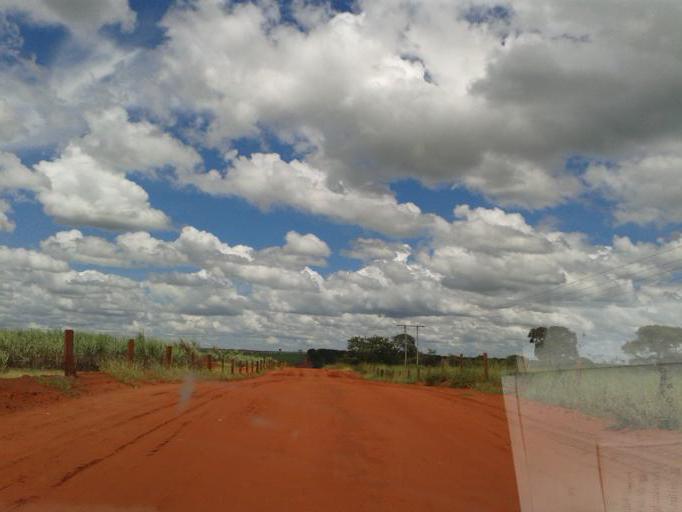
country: BR
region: Minas Gerais
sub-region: Santa Vitoria
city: Santa Vitoria
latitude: -18.8285
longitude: -50.0674
